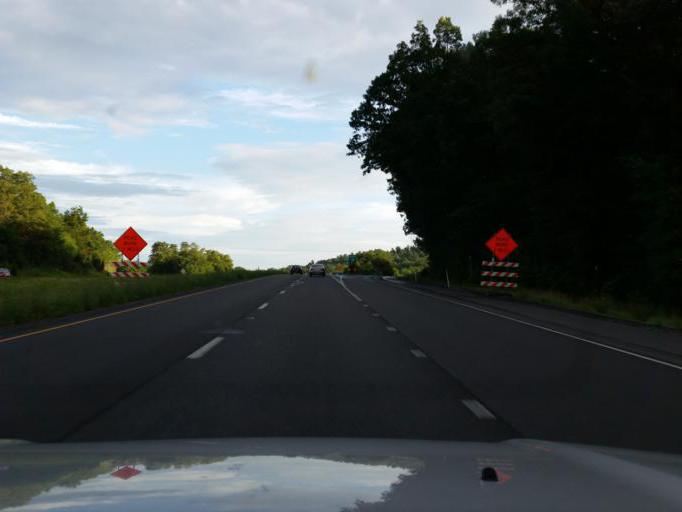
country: US
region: Pennsylvania
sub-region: Adams County
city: Lake Heritage
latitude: 39.8283
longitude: -77.1975
